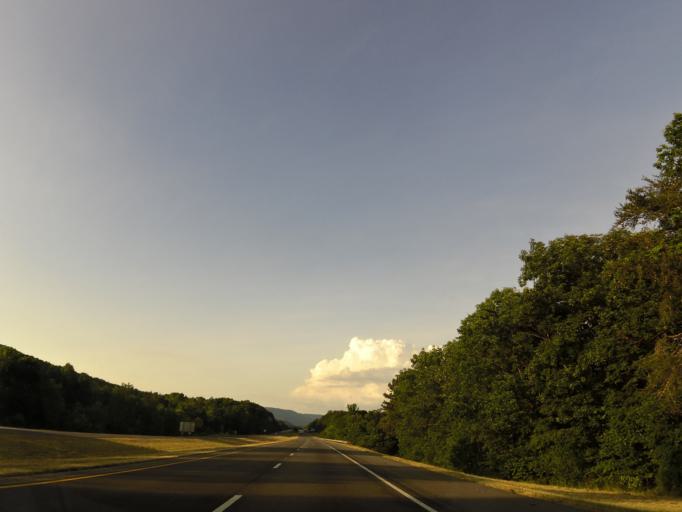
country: US
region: Georgia
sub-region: Dade County
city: Trenton
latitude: 34.7090
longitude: -85.5576
